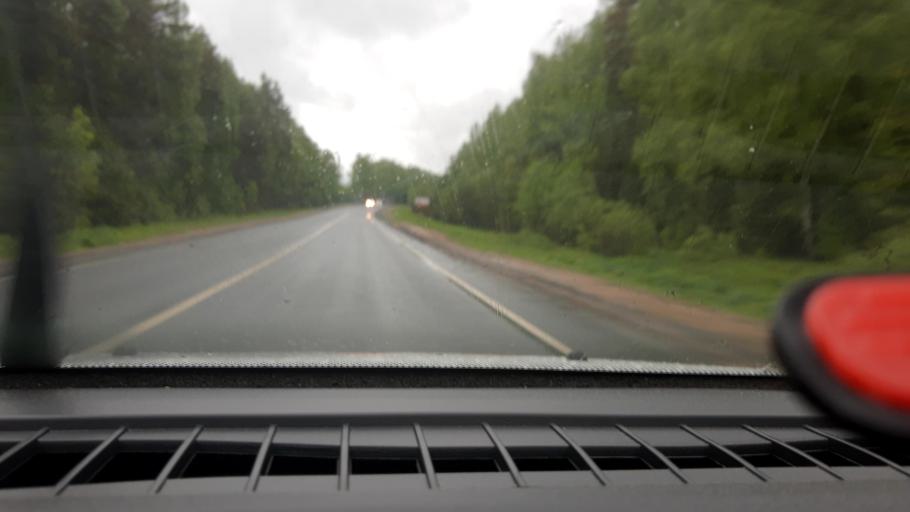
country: RU
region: Nizjnij Novgorod
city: Linda
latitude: 56.7020
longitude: 44.2165
